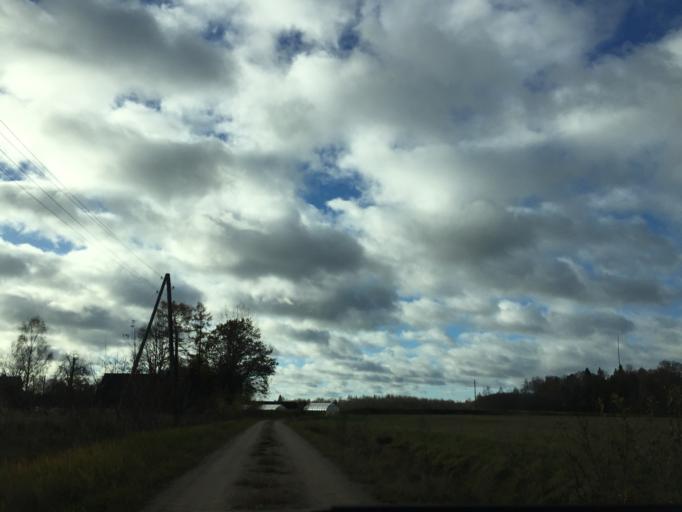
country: LV
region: Engure
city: Smarde
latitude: 56.9634
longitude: 23.2558
